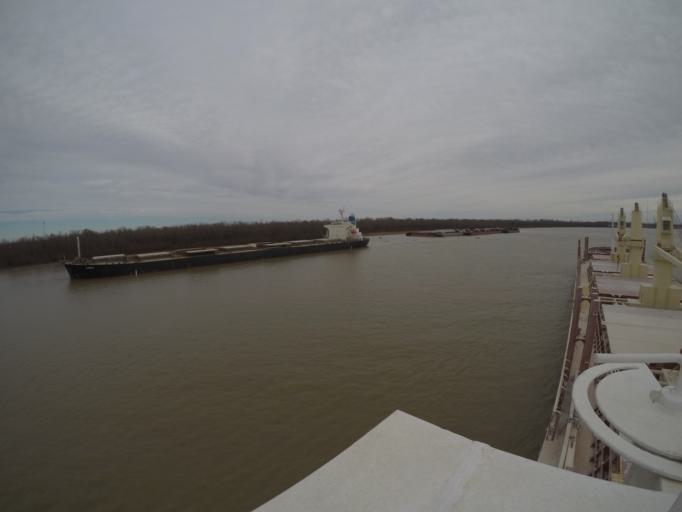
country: US
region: Louisiana
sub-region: Saint John the Baptist Parish
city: Montegut
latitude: 30.0524
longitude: -90.4953
